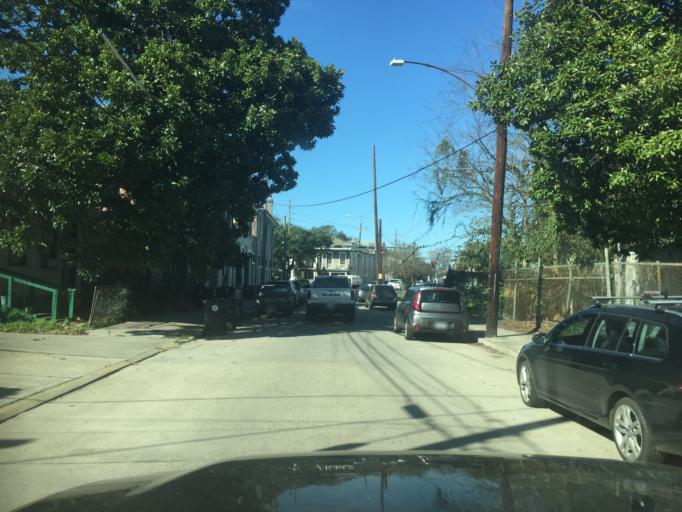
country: US
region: Louisiana
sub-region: Orleans Parish
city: New Orleans
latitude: 29.9374
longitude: -90.0720
